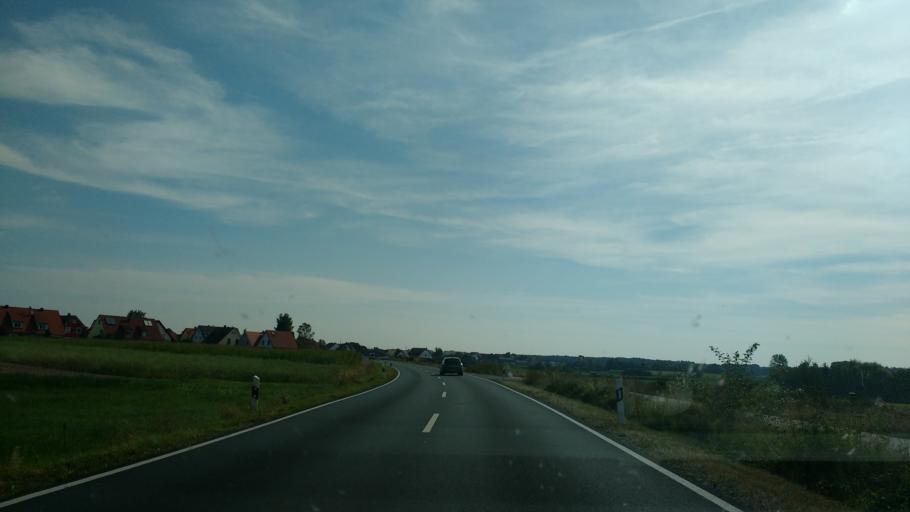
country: DE
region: Bavaria
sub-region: Regierungsbezirk Mittelfranken
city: Grossenseebach
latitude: 49.6307
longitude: 10.8643
